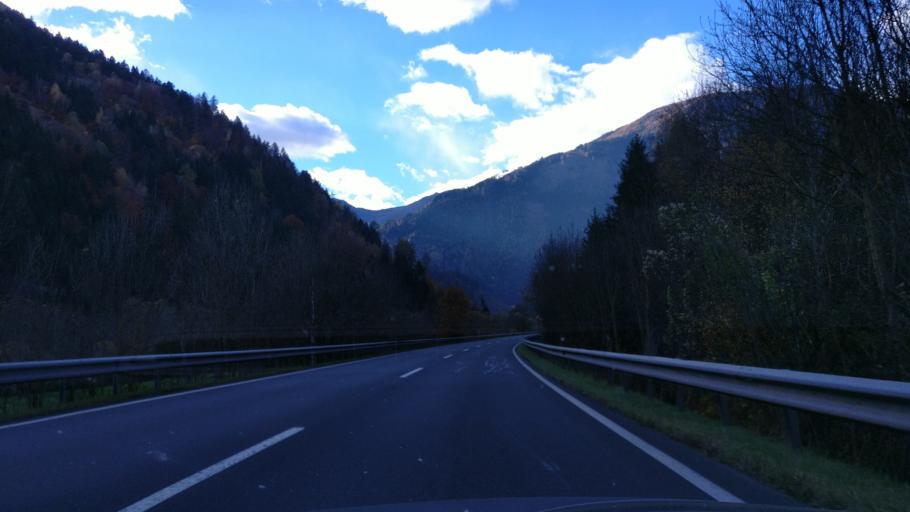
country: AT
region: Carinthia
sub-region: Politischer Bezirk Spittal an der Drau
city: Sachsenburg
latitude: 46.8279
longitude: 13.3712
